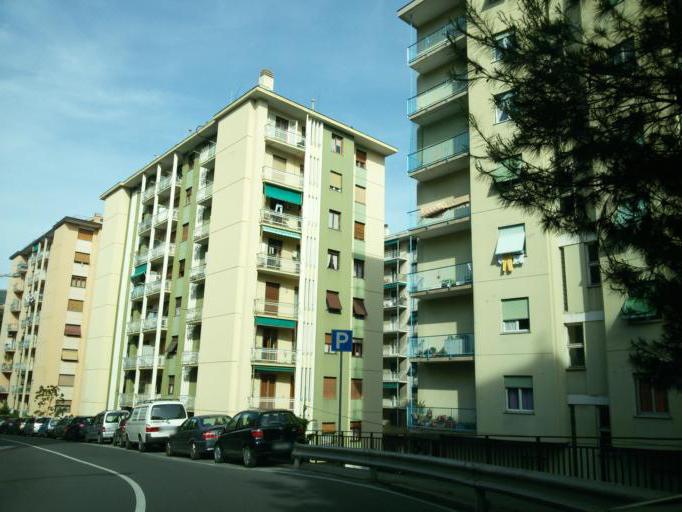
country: IT
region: Liguria
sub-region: Provincia di Genova
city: Genoa
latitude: 44.4188
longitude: 8.9624
